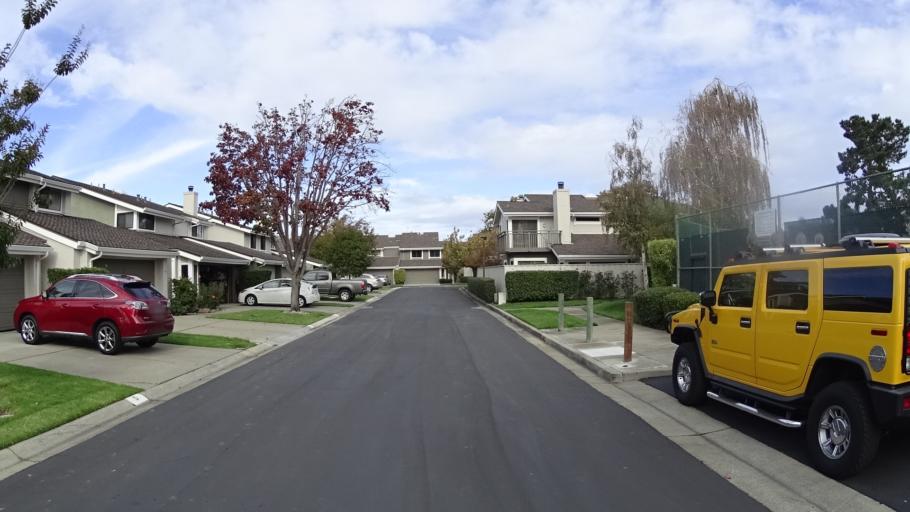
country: US
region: California
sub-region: San Mateo County
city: Redwood Shores
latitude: 37.5331
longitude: -122.2484
